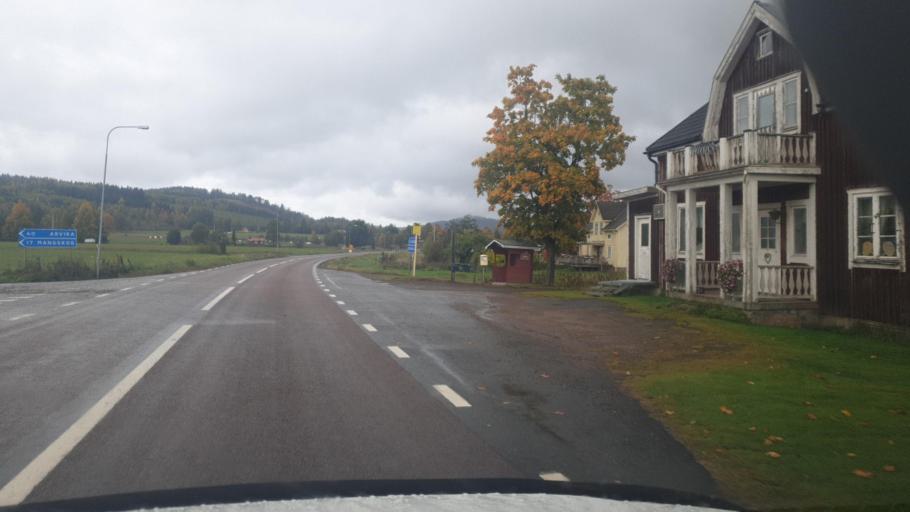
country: SE
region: Vaermland
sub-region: Sunne Kommun
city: Sunne
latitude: 59.8480
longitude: 12.9448
